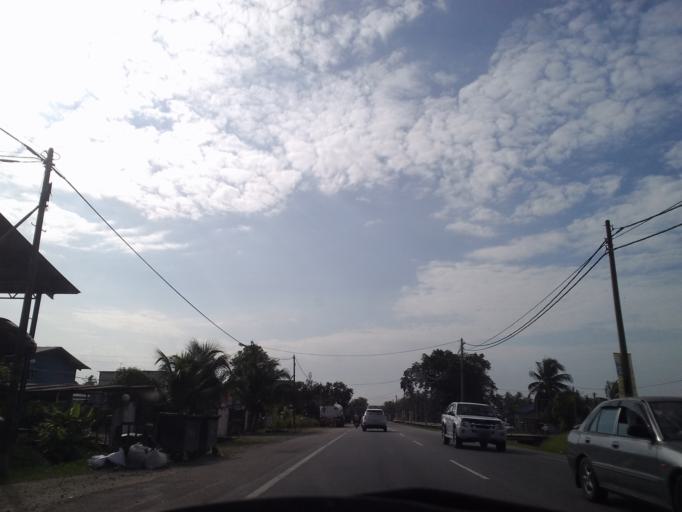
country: MY
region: Kedah
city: Alor Setar
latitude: 6.0397
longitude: 100.3763
